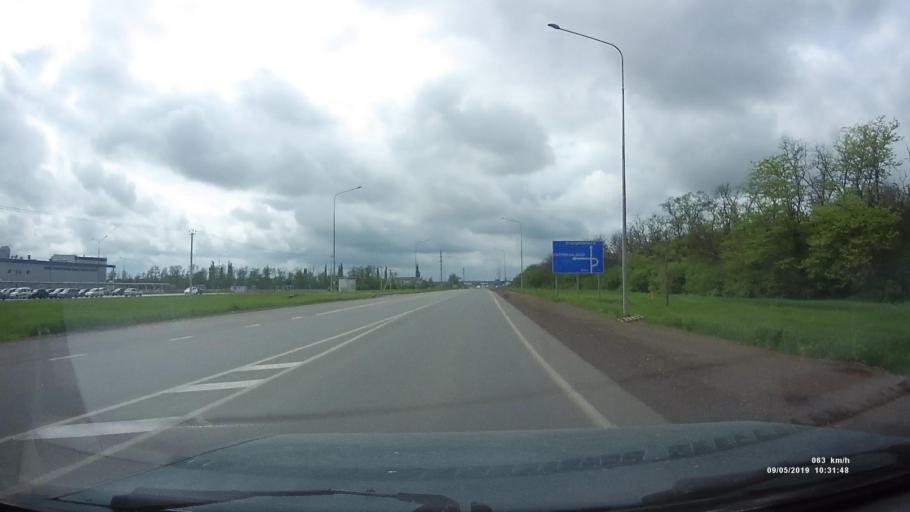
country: RU
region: Rostov
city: Azov
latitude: 47.0785
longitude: 39.4272
